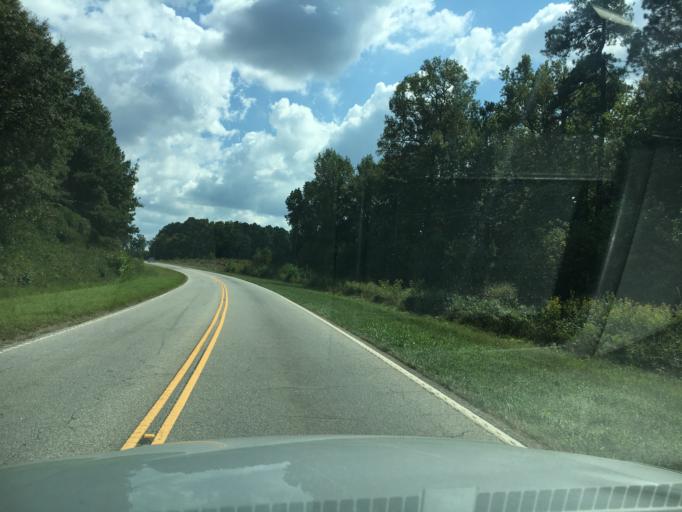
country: US
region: South Carolina
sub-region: Greenwood County
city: Greenwood
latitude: 34.1618
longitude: -82.1820
